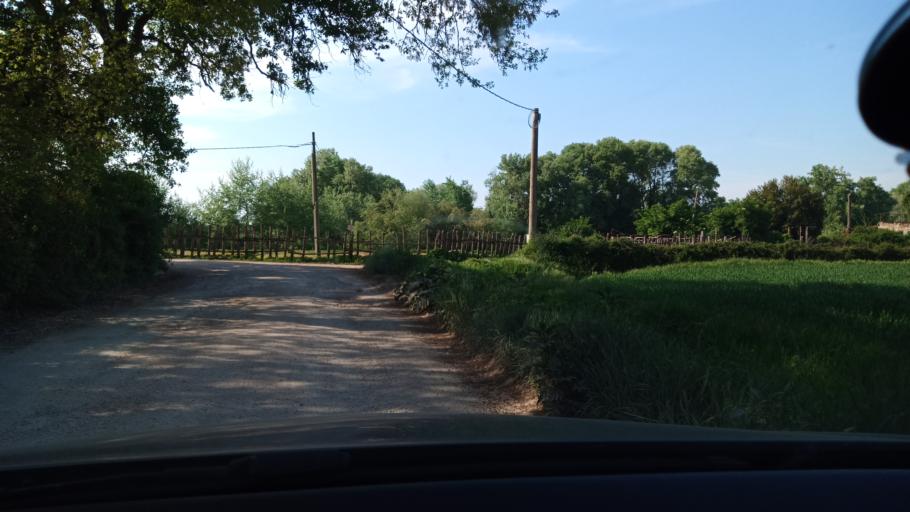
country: IT
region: Latium
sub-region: Citta metropolitana di Roma Capitale
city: Ponzano Romano
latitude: 42.2681
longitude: 12.5600
